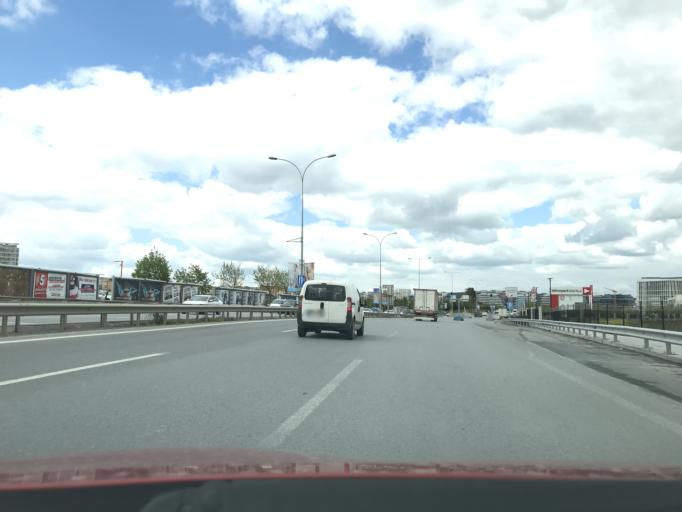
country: TR
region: Istanbul
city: Pendik
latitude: 40.9167
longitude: 29.3120
